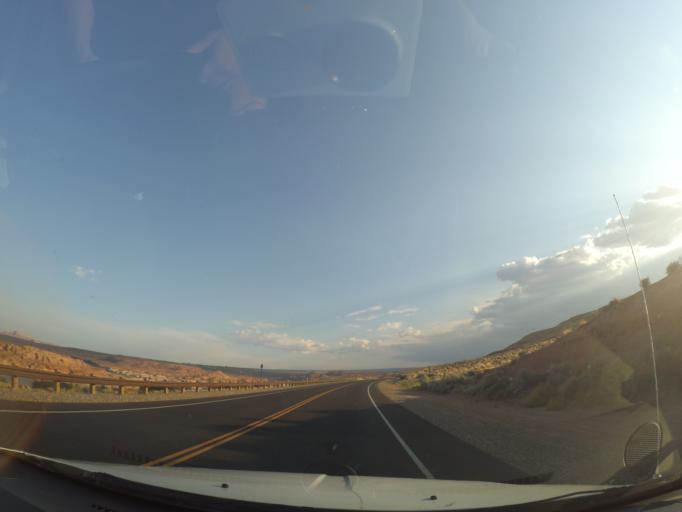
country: US
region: Arizona
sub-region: Coconino County
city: Page
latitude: 36.9675
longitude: -111.4898
